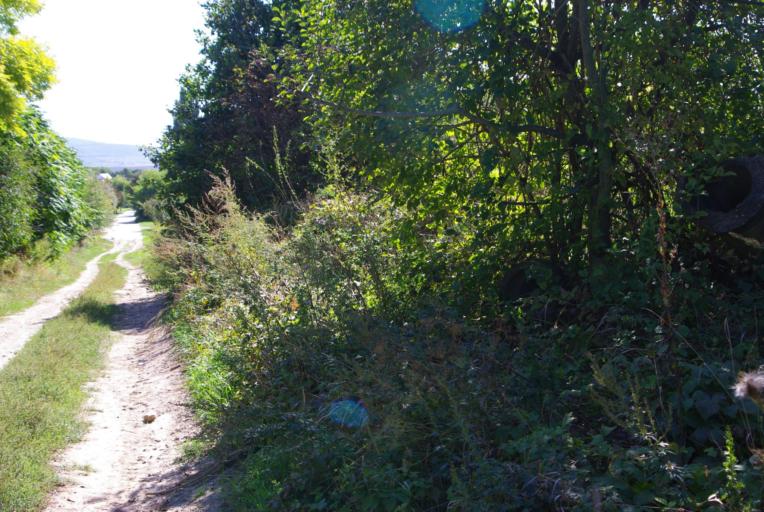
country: HU
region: Pest
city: Perbal
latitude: 47.5931
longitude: 18.7493
